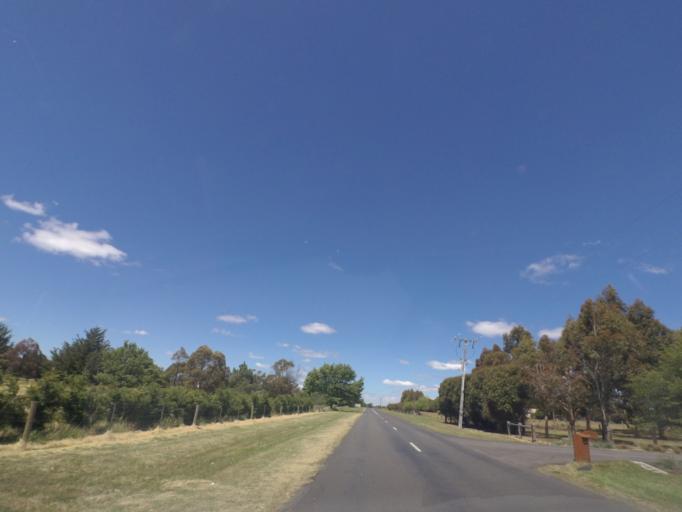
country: AU
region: Victoria
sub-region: Mount Alexander
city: Castlemaine
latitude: -37.2368
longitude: 144.4059
